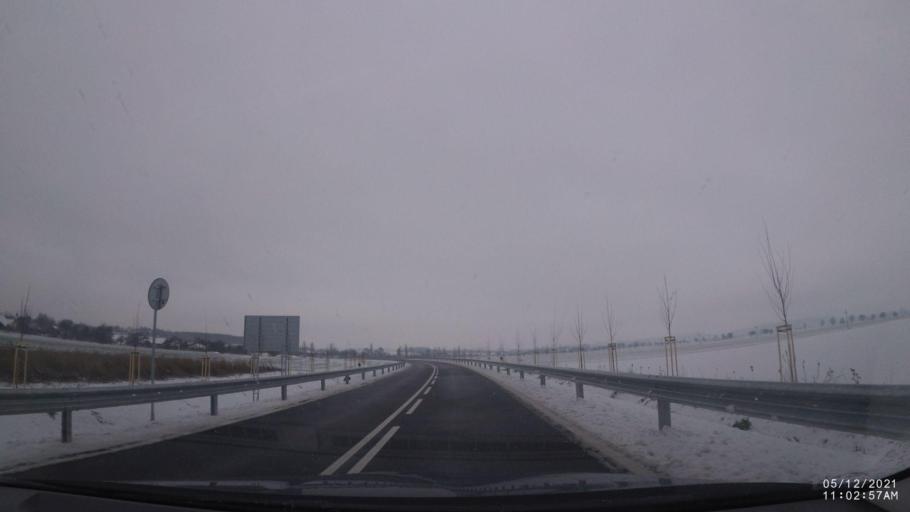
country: CZ
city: Solnice
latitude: 50.1822
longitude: 16.2192
